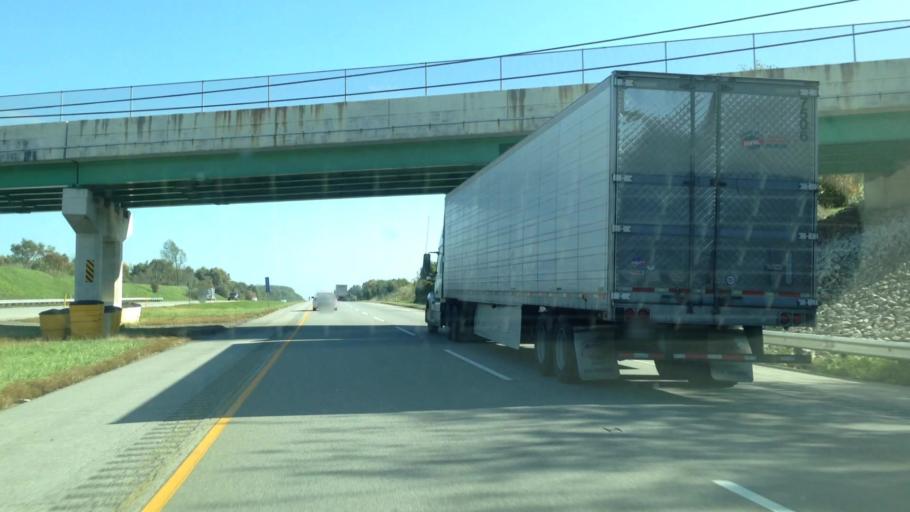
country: US
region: Indiana
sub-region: LaPorte County
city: Westville
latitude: 41.6083
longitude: -86.8524
